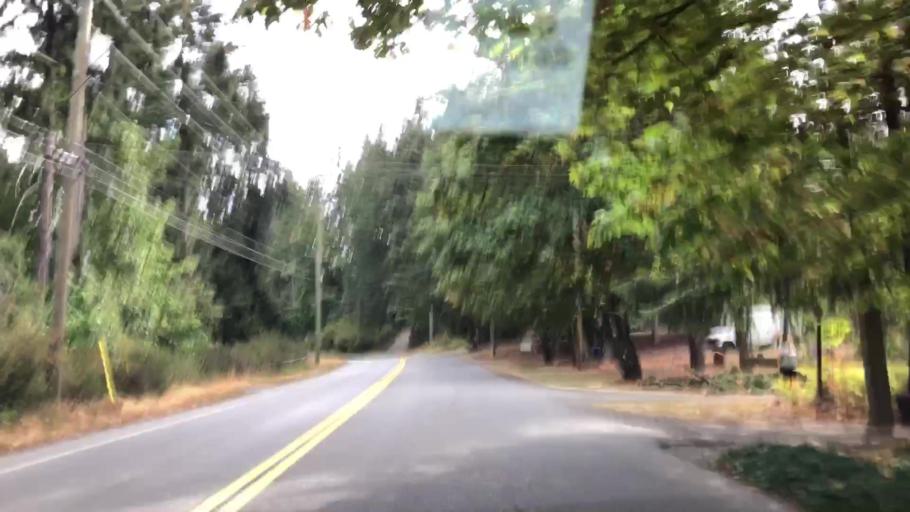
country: CA
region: British Columbia
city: North Saanich
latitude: 48.6865
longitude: -123.5731
